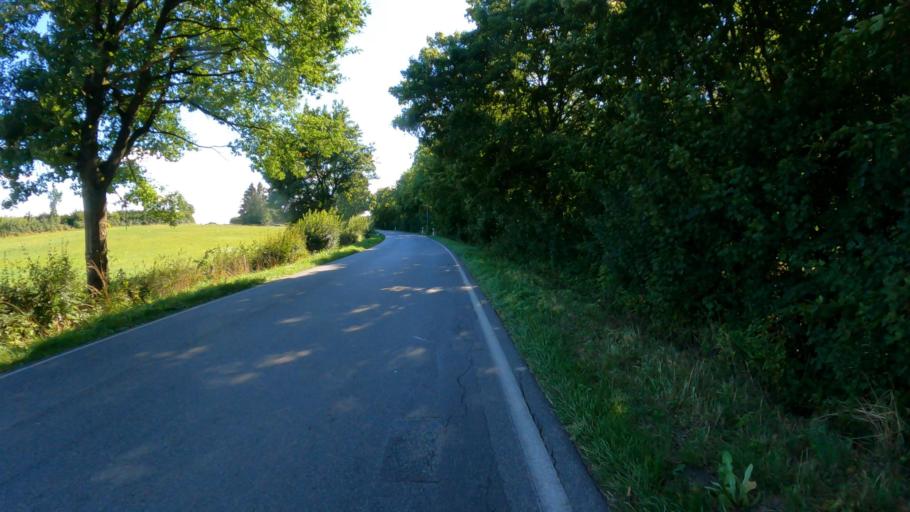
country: DE
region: Schleswig-Holstein
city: Stubben
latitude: 53.7386
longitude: 10.4417
